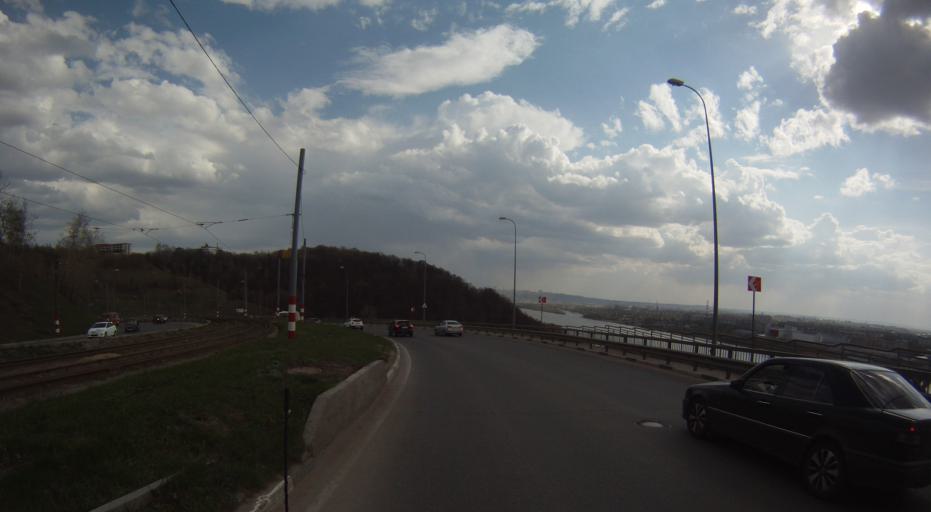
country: RU
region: Nizjnij Novgorod
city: Nizhniy Novgorod
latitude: 56.3014
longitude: 43.9704
